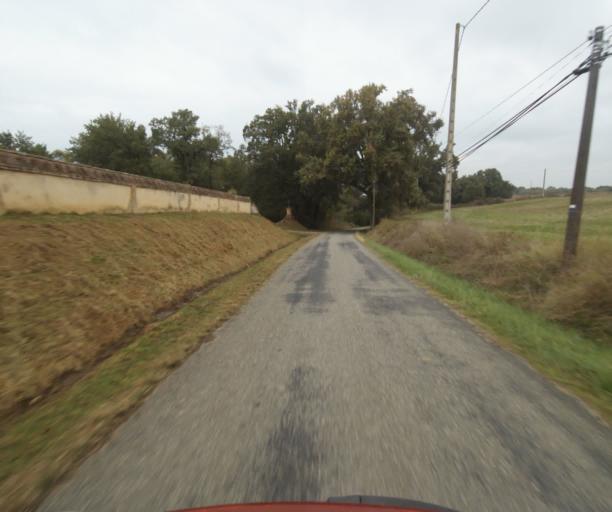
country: FR
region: Midi-Pyrenees
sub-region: Departement du Tarn-et-Garonne
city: Verdun-sur-Garonne
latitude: 43.8355
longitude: 1.1953
